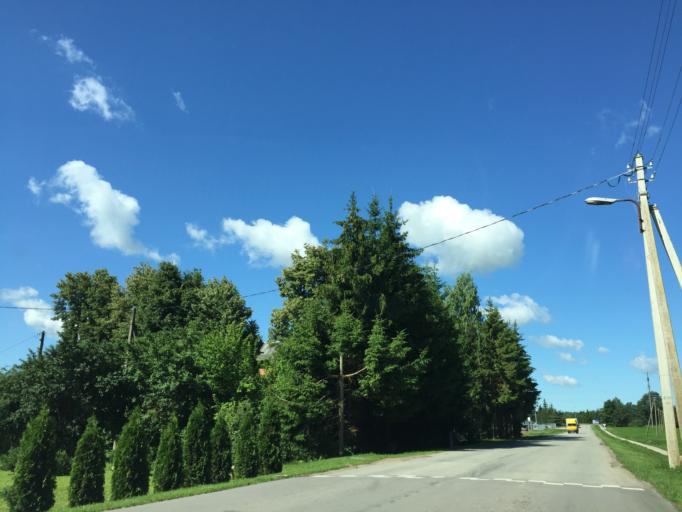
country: LT
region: Panevezys
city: Pasvalys
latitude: 56.0694
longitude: 24.4409
